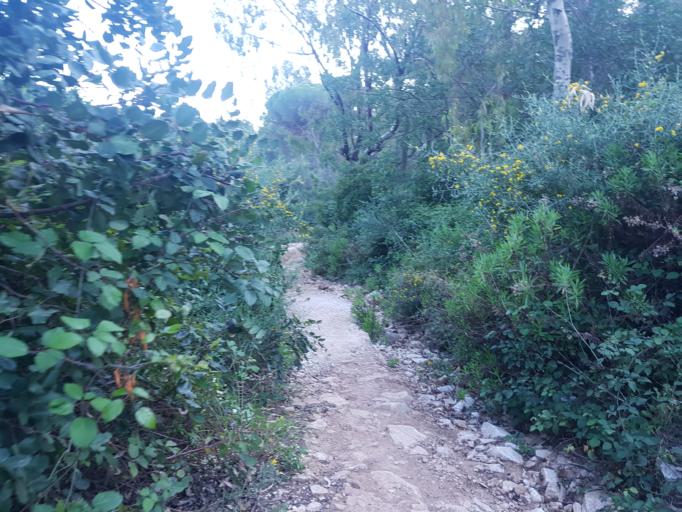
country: ES
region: Andalusia
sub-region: Provincia de Malaga
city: Marbella
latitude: 36.5414
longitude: -4.8846
